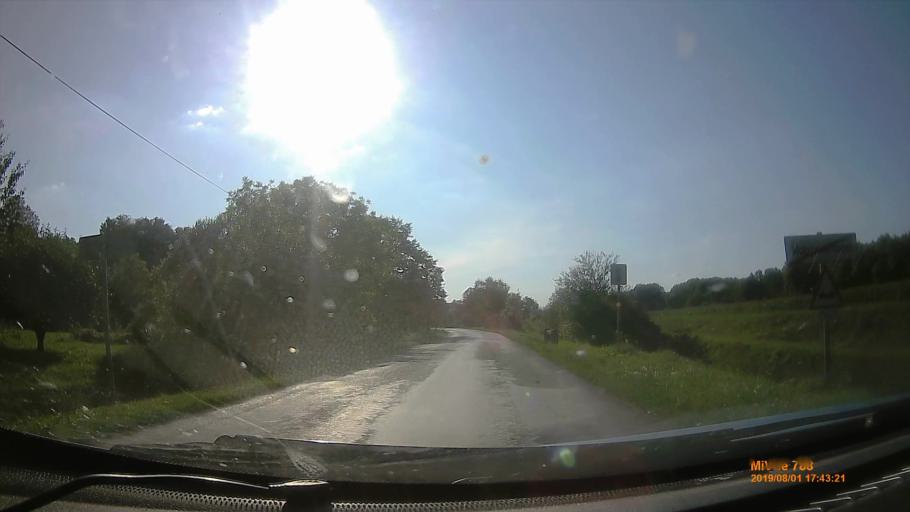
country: HU
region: Baranya
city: Sasd
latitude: 46.1921
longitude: 18.1510
